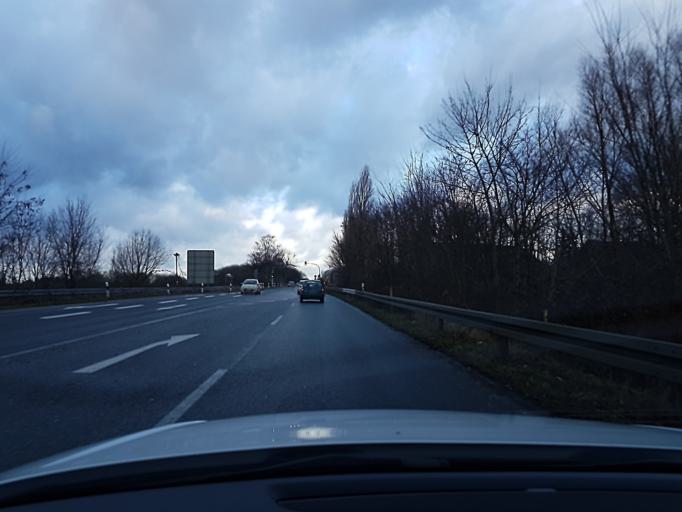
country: DE
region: North Rhine-Westphalia
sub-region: Regierungsbezirk Dusseldorf
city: Ratingen
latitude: 51.3565
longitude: 6.8634
